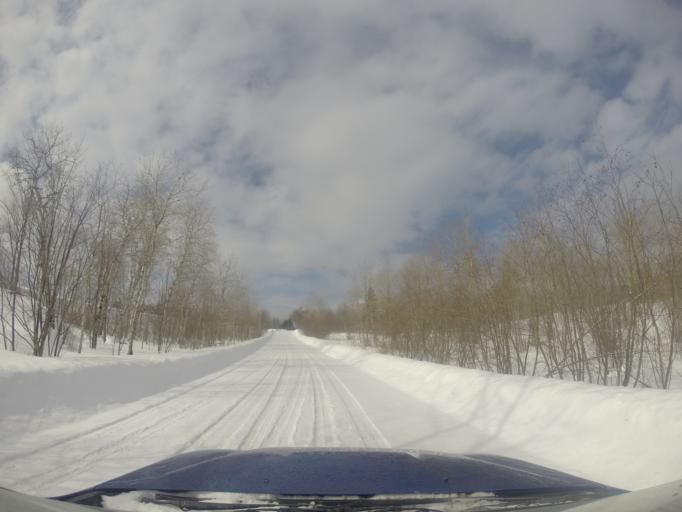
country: CA
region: Ontario
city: Greater Sudbury
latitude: 46.1050
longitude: -80.6731
